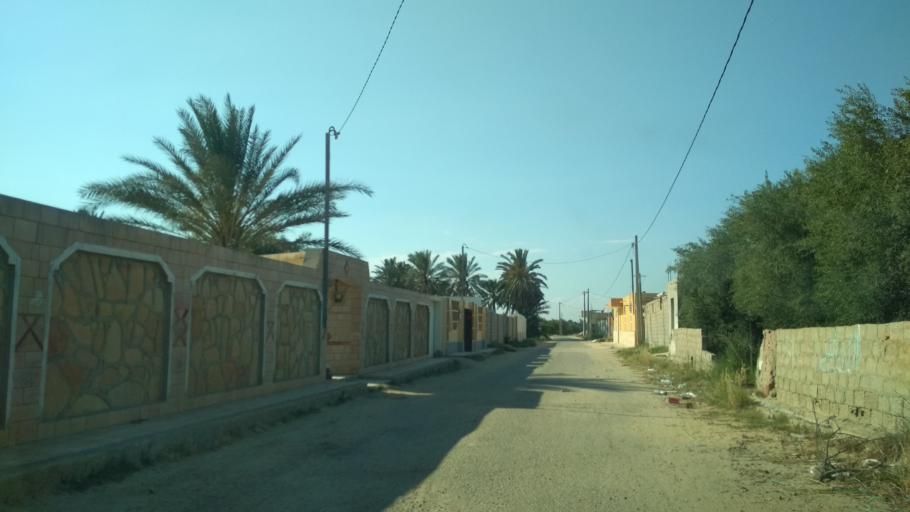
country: TN
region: Qabis
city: Gabes
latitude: 33.9492
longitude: 10.0612
